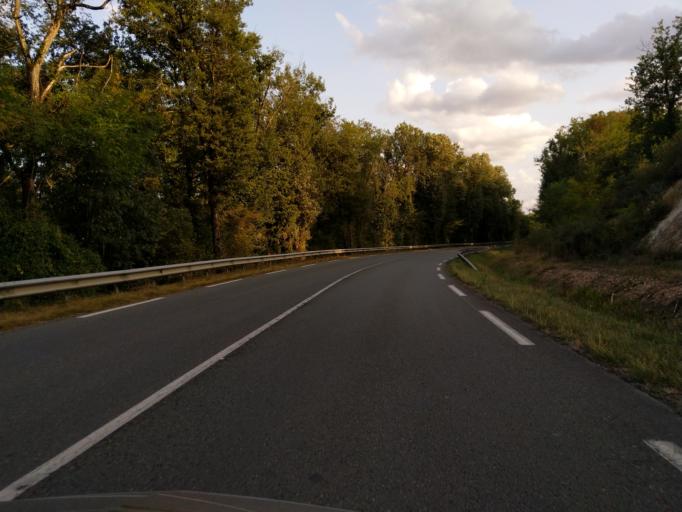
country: FR
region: Midi-Pyrenees
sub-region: Departement du Tarn
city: Realmont
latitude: 43.7937
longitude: 2.1881
